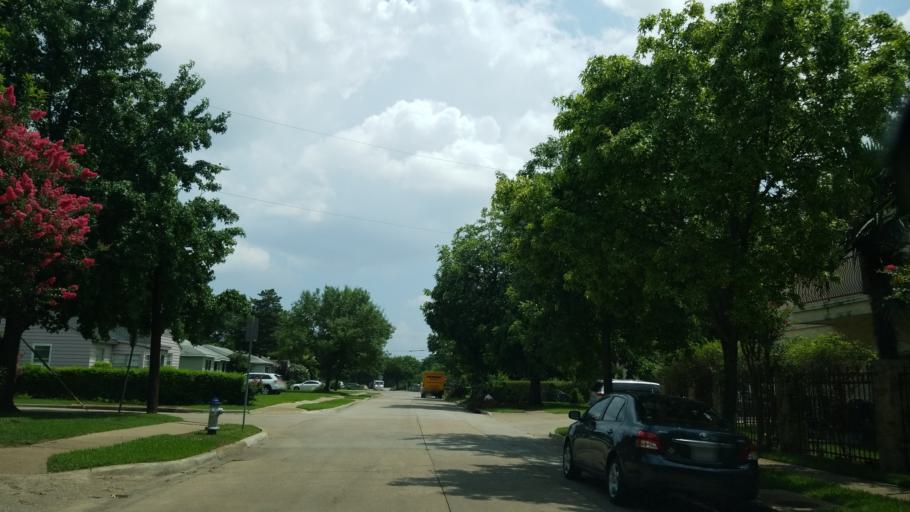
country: US
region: Texas
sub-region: Dallas County
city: University Park
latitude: 32.8505
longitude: -96.8287
